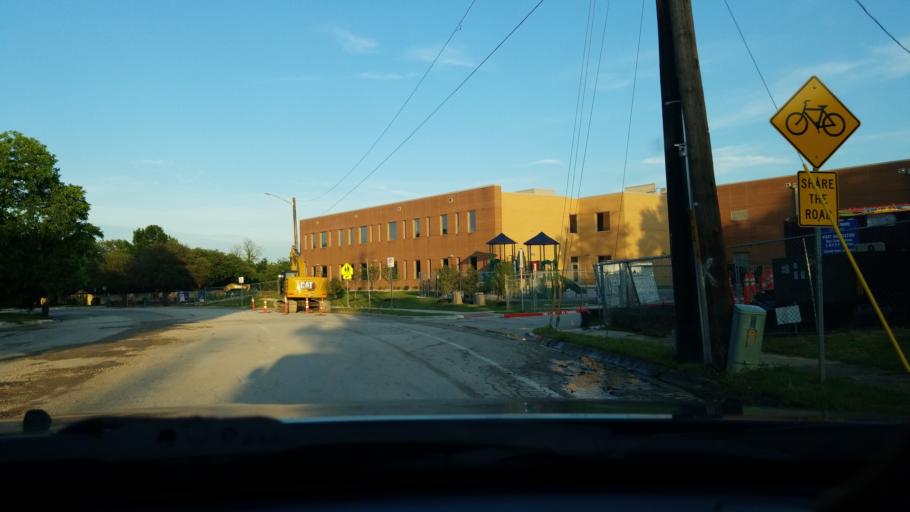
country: US
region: Texas
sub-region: Denton County
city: Denton
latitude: 33.2428
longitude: -97.1150
